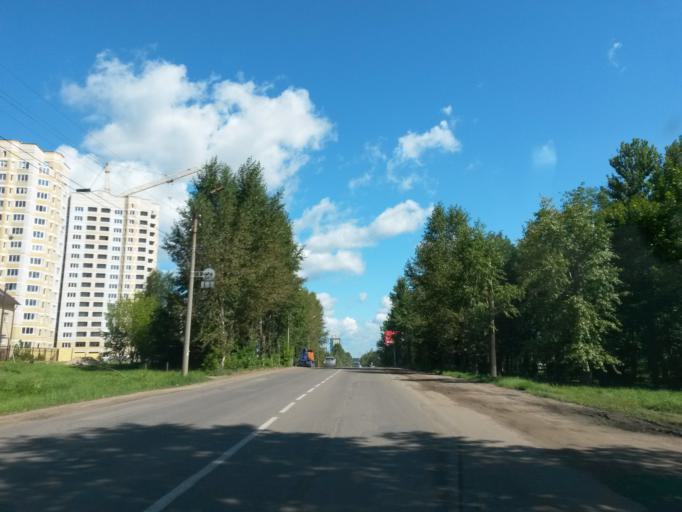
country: RU
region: Jaroslavl
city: Yaroslavl
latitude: 57.5773
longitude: 39.8679
